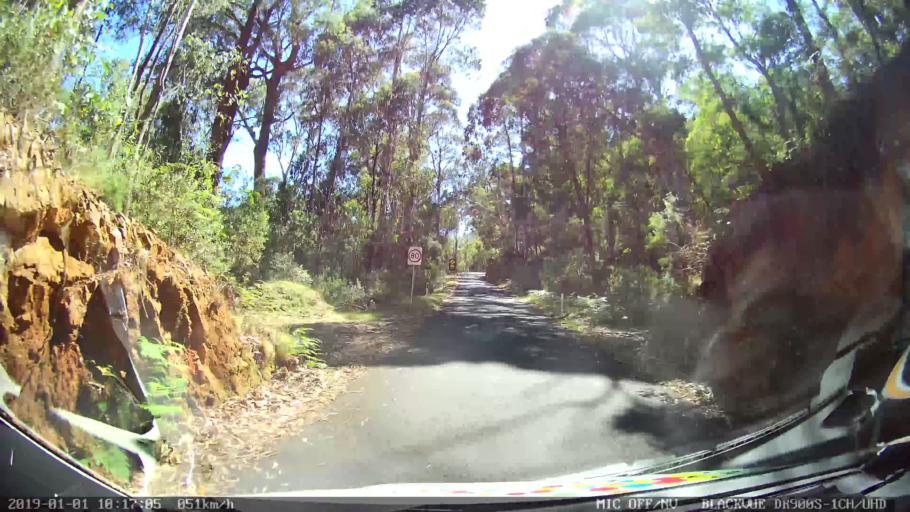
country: AU
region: New South Wales
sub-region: Snowy River
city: Jindabyne
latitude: -36.0918
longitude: 148.1731
